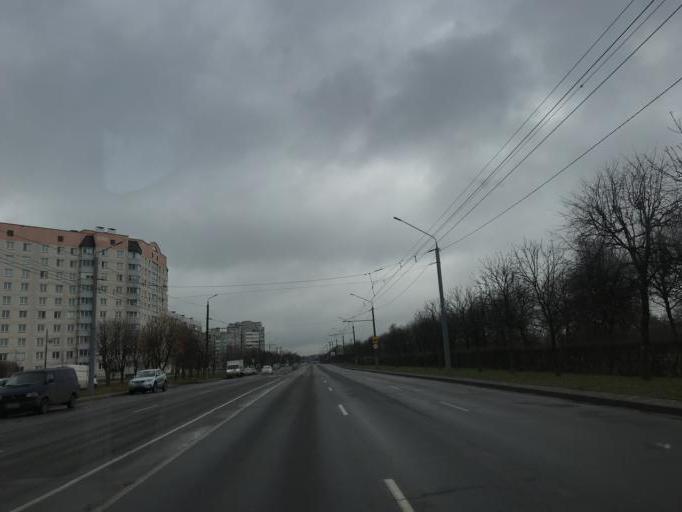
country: BY
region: Mogilev
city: Mahilyow
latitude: 53.8681
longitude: 30.3275
